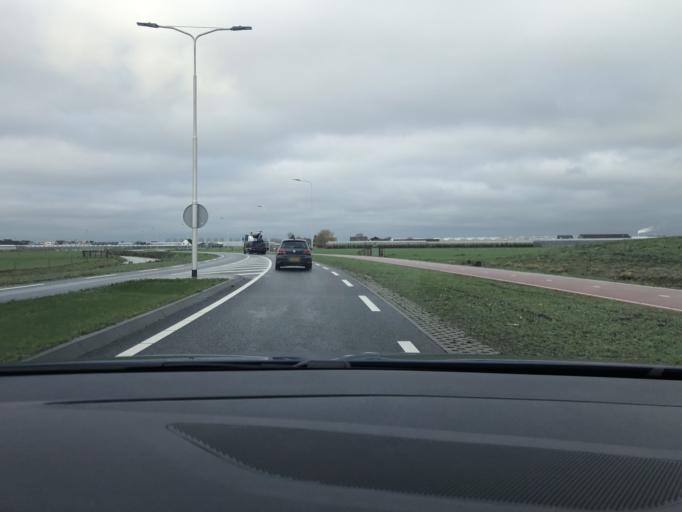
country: NL
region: South Holland
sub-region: Gemeente Pijnacker-Nootdorp
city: Pijnacker
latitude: 52.0177
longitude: 4.4555
